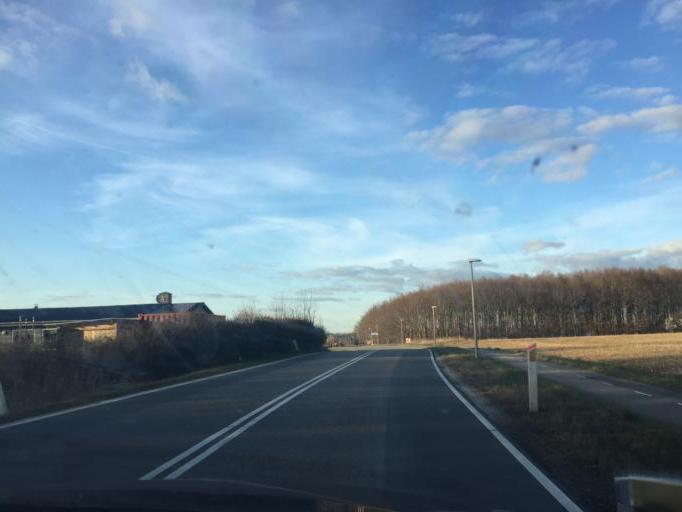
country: DK
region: Capital Region
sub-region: Hoje-Taastrup Kommune
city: Flong
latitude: 55.6354
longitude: 12.1936
